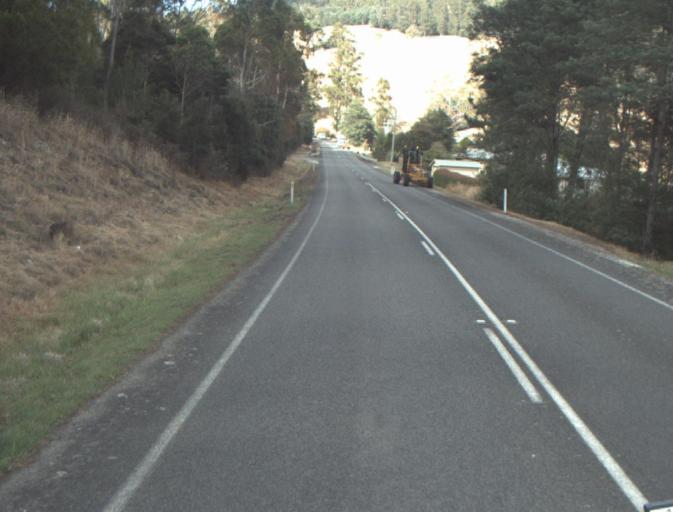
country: AU
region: Tasmania
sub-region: Launceston
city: Mayfield
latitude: -41.2647
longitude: 147.2159
